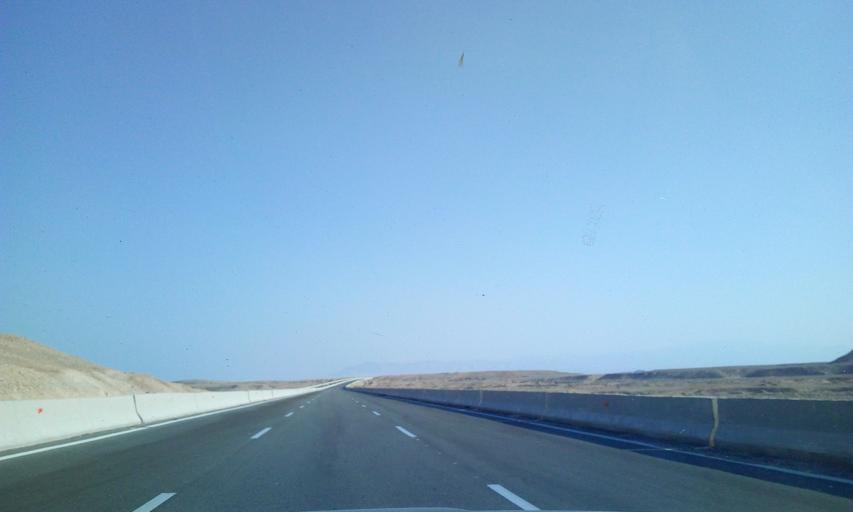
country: EG
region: As Suways
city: Ain Sukhna
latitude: 29.2231
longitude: 32.4895
